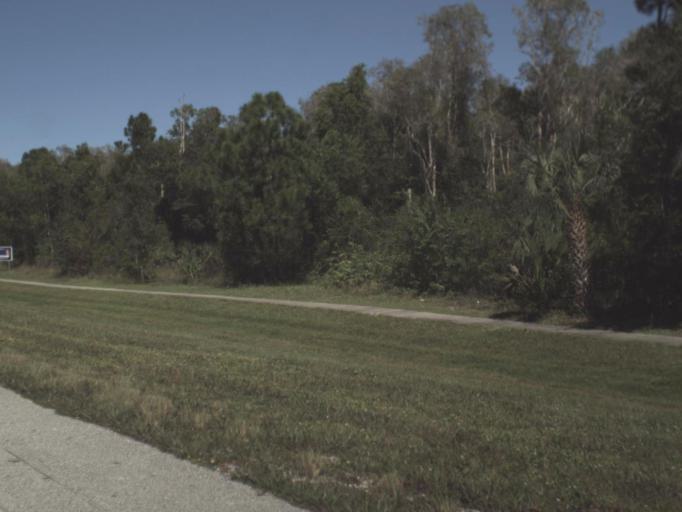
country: US
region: Florida
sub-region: Lee County
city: San Carlos Park
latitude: 26.4793
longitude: -81.8385
